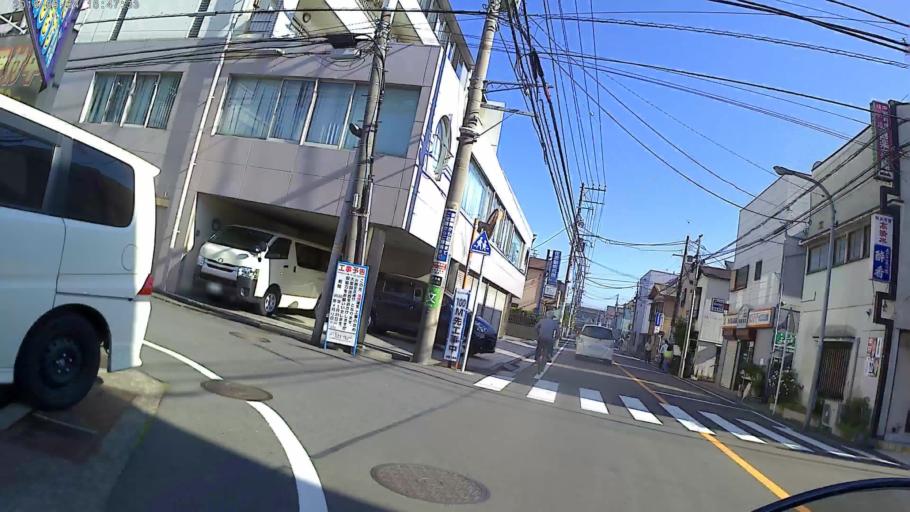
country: JP
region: Kanagawa
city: Yokohama
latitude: 35.4985
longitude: 139.6462
